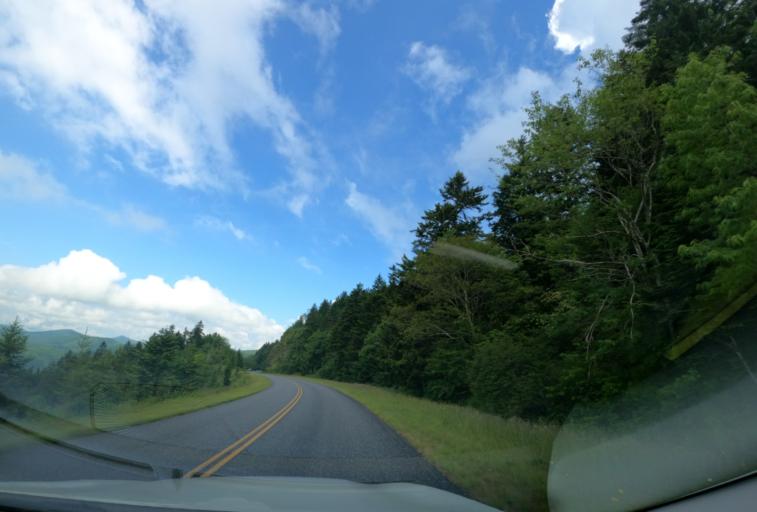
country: US
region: North Carolina
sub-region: Haywood County
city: Hazelwood
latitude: 35.3719
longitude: -82.9981
